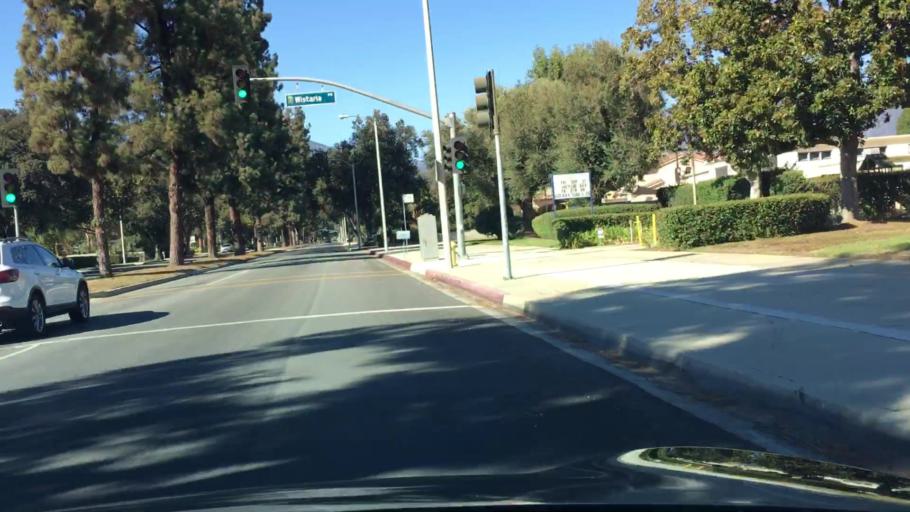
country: US
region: California
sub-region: Los Angeles County
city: North El Monte
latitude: 34.1172
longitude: -118.0309
